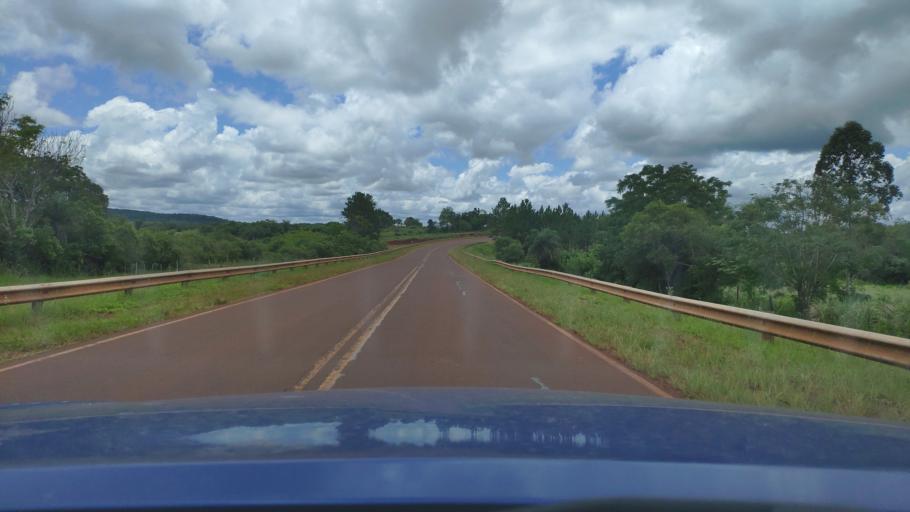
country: AR
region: Misiones
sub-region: Departamento de San Javier
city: San Javier
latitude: -27.8454
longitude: -55.2424
